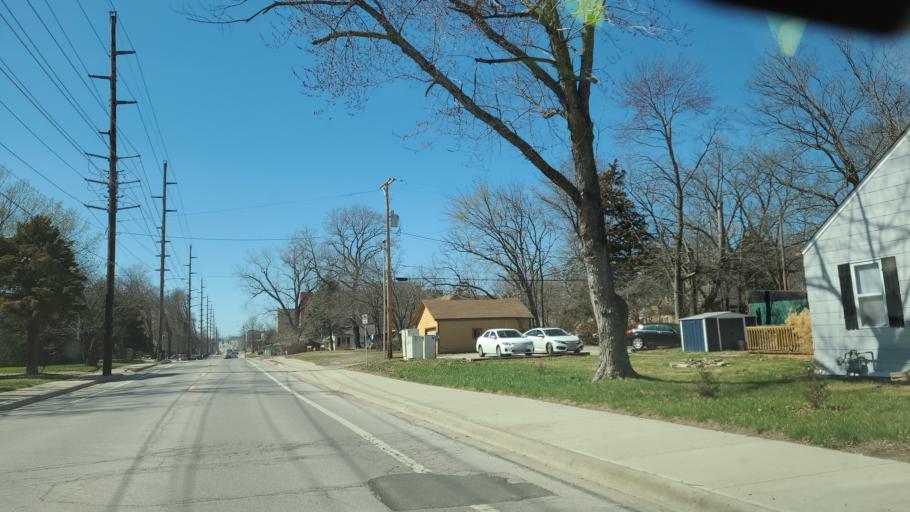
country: US
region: Kansas
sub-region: Douglas County
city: Lawrence
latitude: 38.9501
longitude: -95.2467
